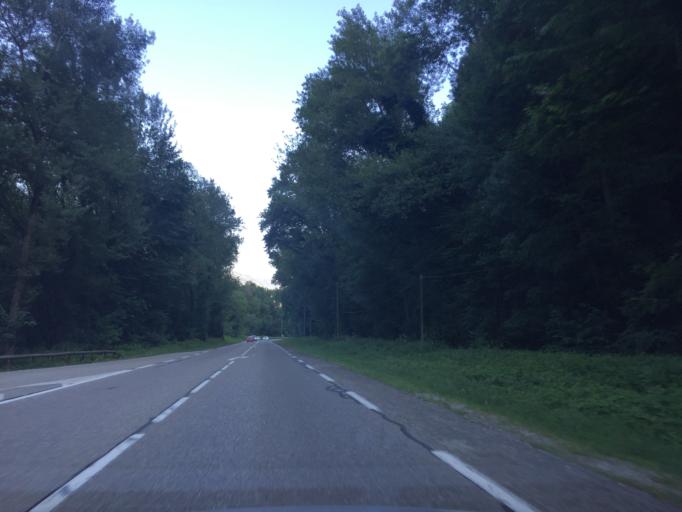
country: FR
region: Rhone-Alpes
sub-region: Departement de l'Isere
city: Voreppe
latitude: 45.2971
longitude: 5.6105
